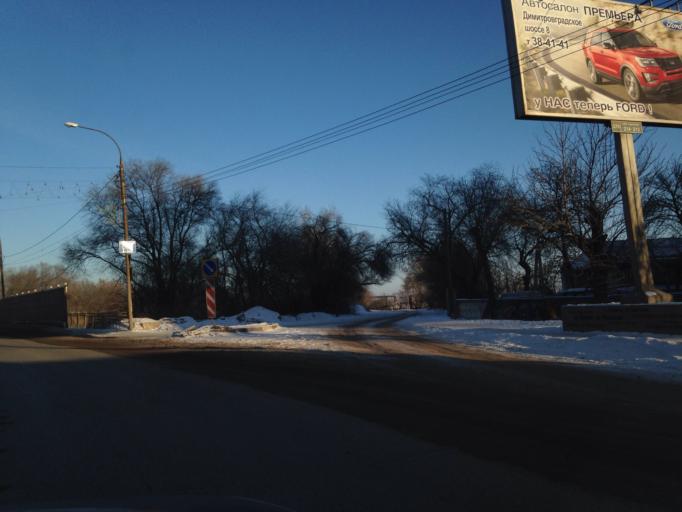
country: RU
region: Ulyanovsk
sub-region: Ulyanovskiy Rayon
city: Ulyanovsk
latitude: 54.2902
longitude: 48.3693
